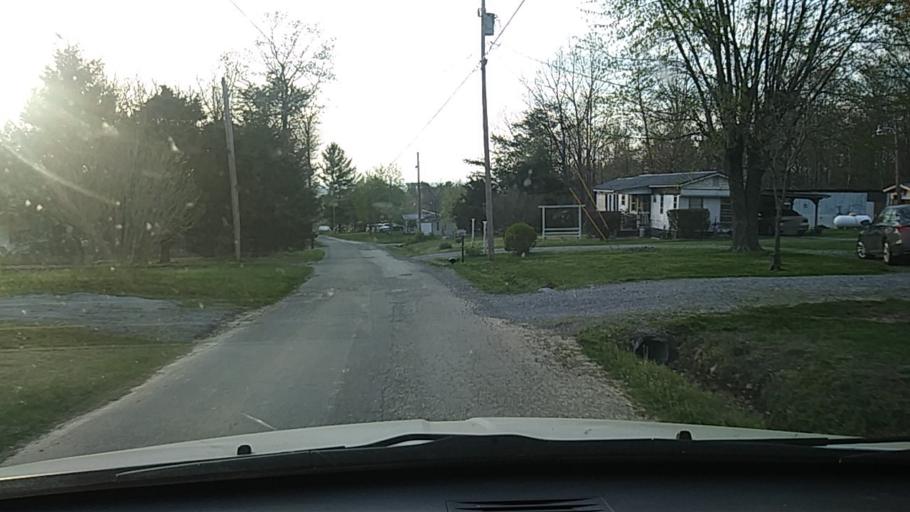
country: US
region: Tennessee
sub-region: Greene County
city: Tusculum
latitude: 36.0928
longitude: -82.6978
